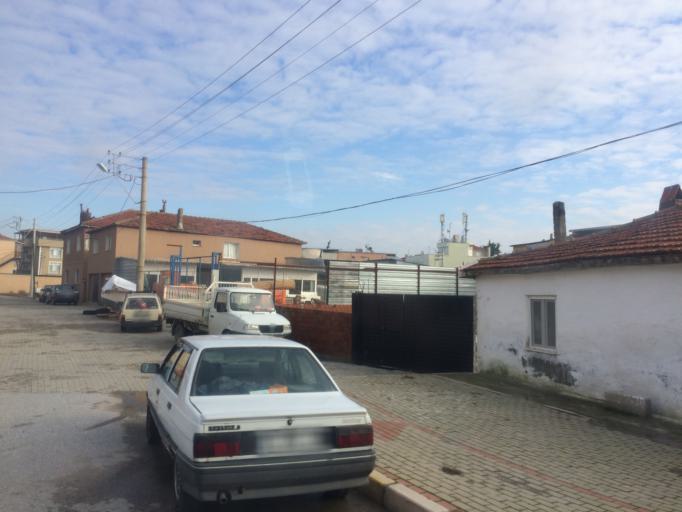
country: TR
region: Izmir
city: Karsiyaka
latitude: 38.4934
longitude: 26.9508
